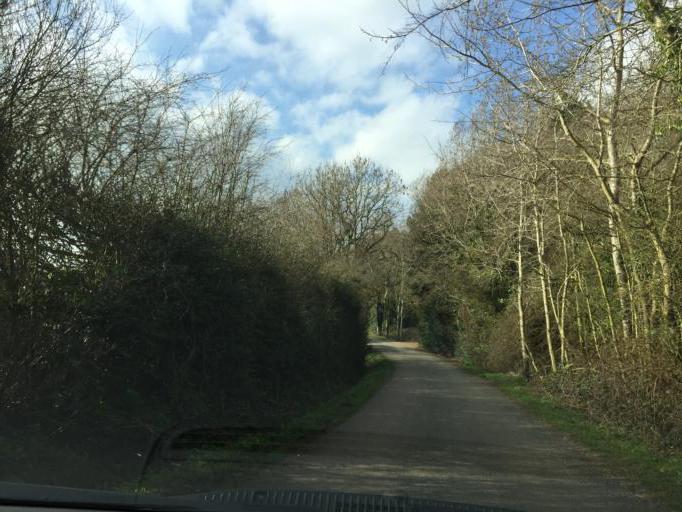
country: GB
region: England
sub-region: Coventry
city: Keresley
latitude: 52.4500
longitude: -1.5869
